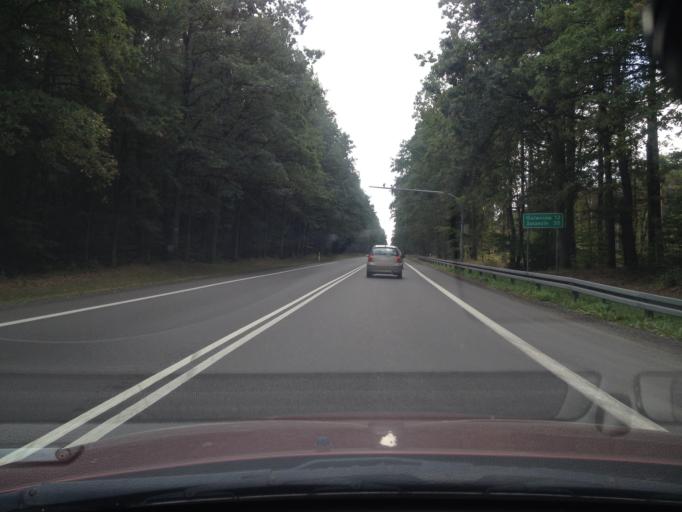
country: PL
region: West Pomeranian Voivodeship
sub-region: Powiat goleniowski
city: Przybiernow
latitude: 53.6746
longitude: 14.8138
